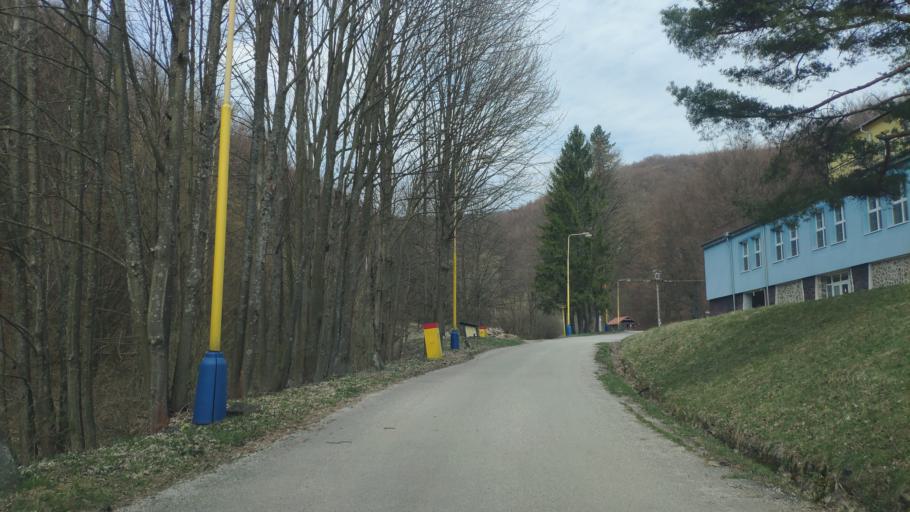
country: SK
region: Kosicky
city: Moldava nad Bodvou
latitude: 48.7474
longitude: 21.0272
